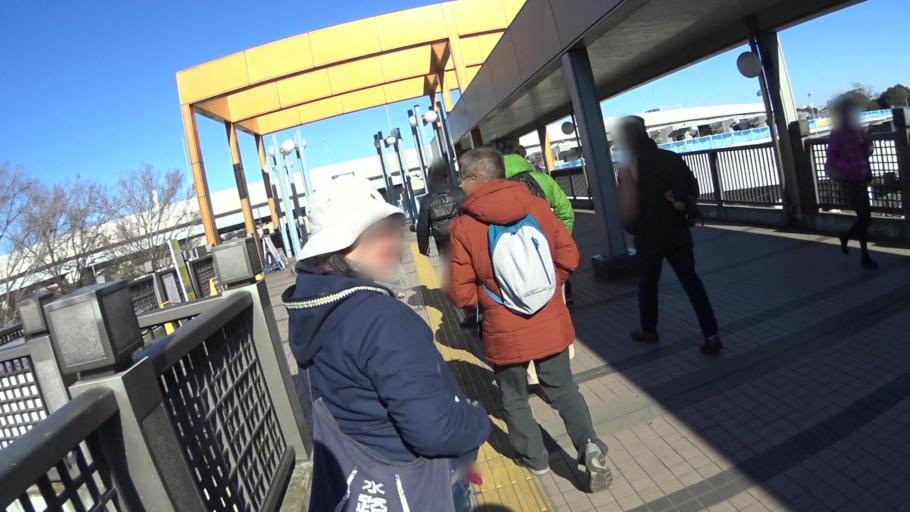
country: JP
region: Tokyo
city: Urayasu
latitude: 35.6384
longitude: 139.8835
